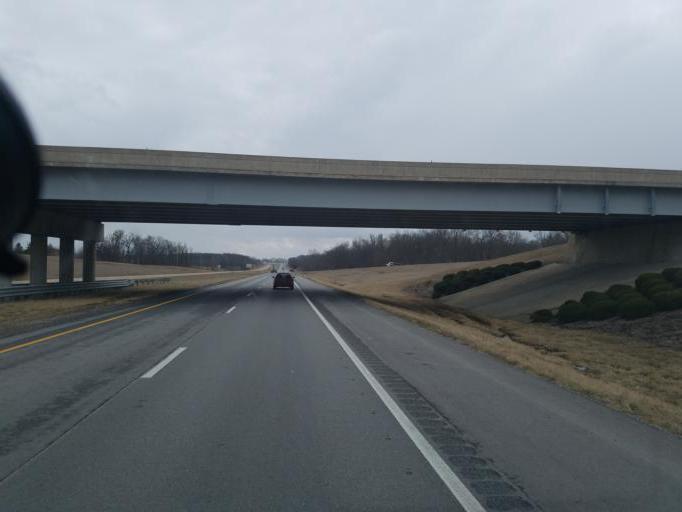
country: US
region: Missouri
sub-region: Randolph County
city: Moberly
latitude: 39.3943
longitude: -92.4131
